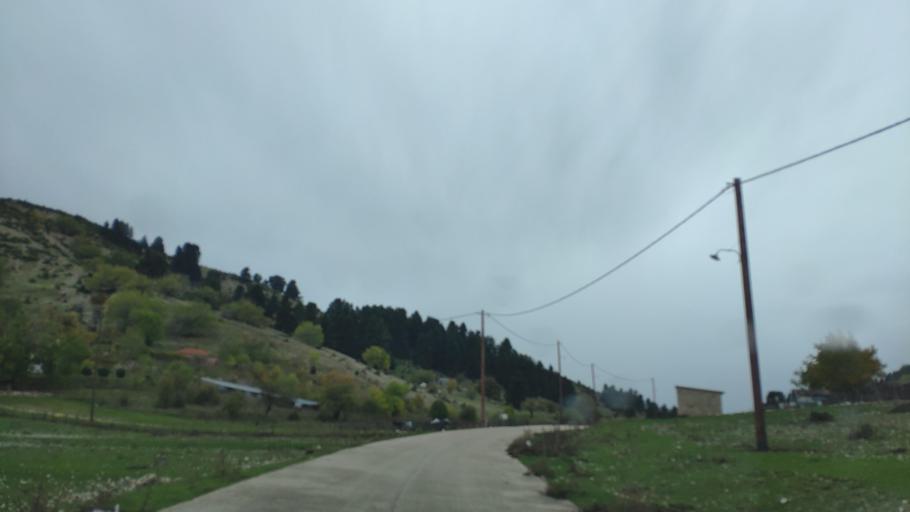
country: GR
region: Epirus
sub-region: Nomos Thesprotias
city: Paramythia
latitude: 39.4473
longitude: 20.6448
